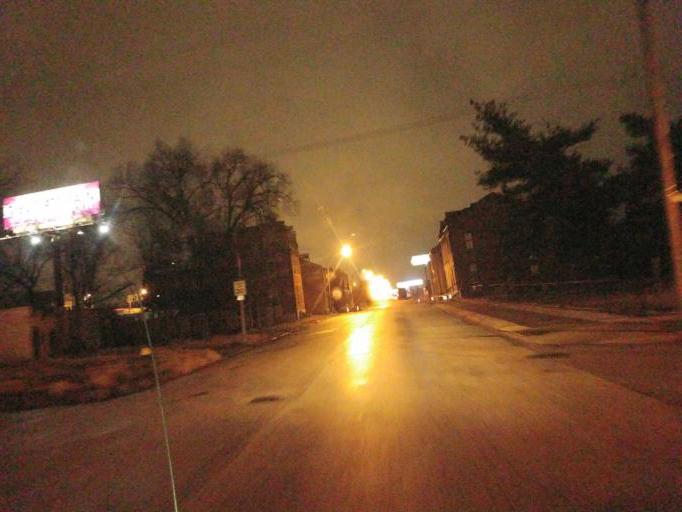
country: US
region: Illinois
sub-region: Madison County
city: Venice
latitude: 38.6581
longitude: -90.1947
